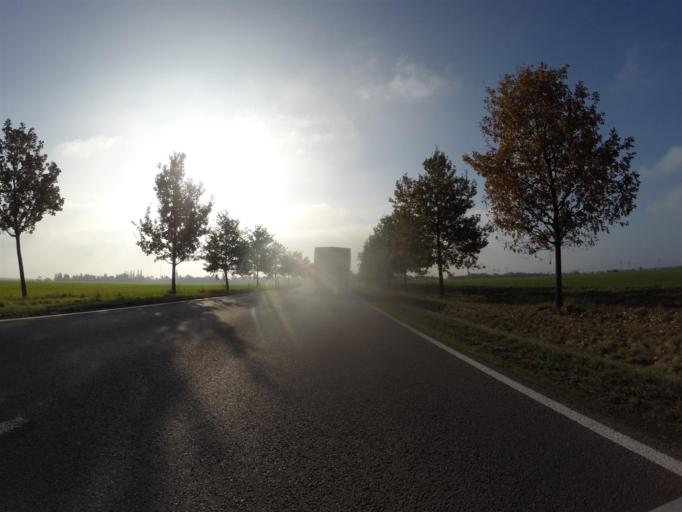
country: DE
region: Saxony
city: Markranstadt
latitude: 51.2791
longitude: 12.2799
